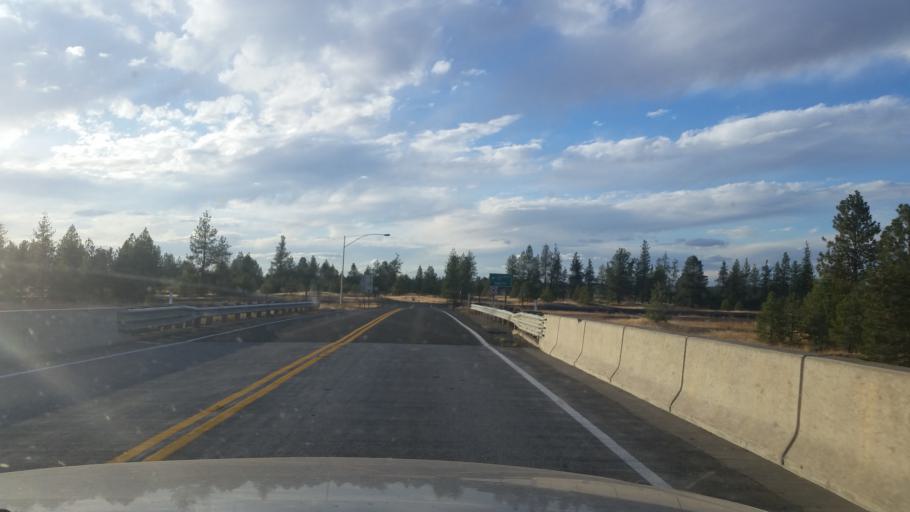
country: US
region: Washington
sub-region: Spokane County
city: Medical Lake
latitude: 47.4362
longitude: -117.7904
